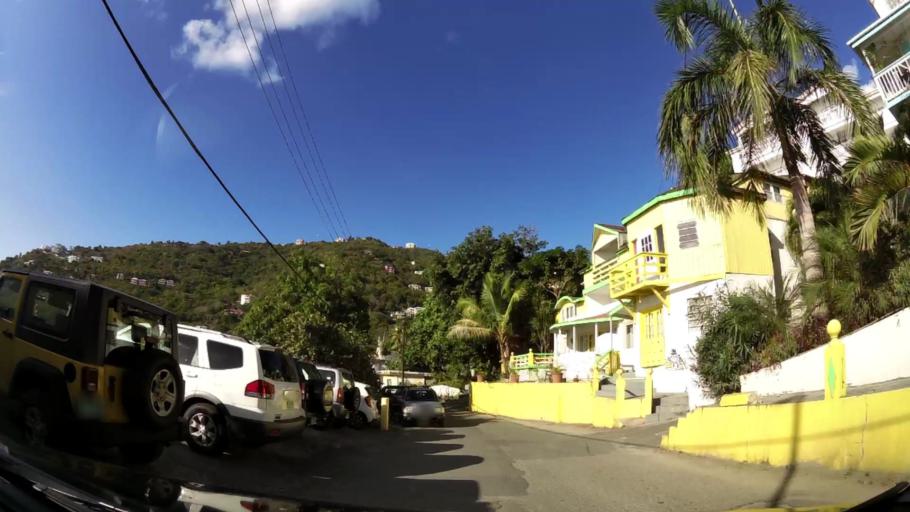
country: VG
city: Road Town
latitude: 18.4279
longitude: -64.6573
